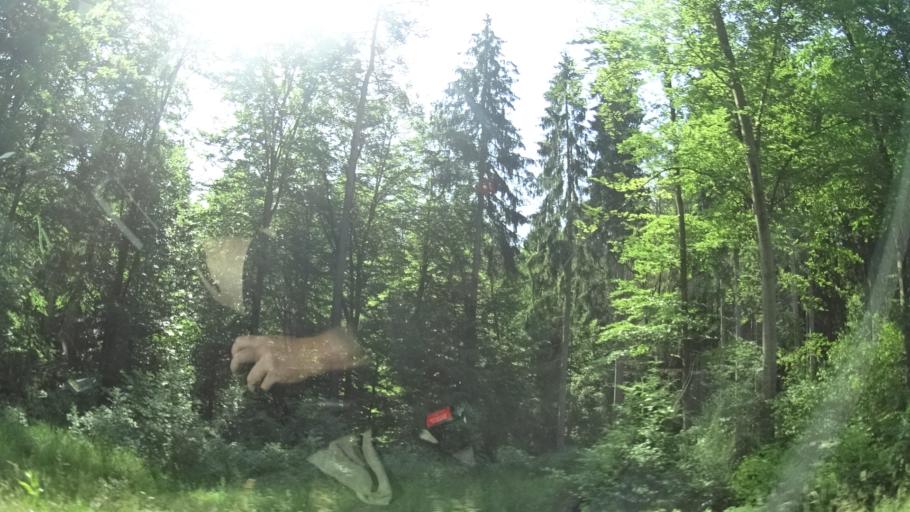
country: DE
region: Hesse
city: Rosenthal
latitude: 50.9548
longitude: 8.8600
